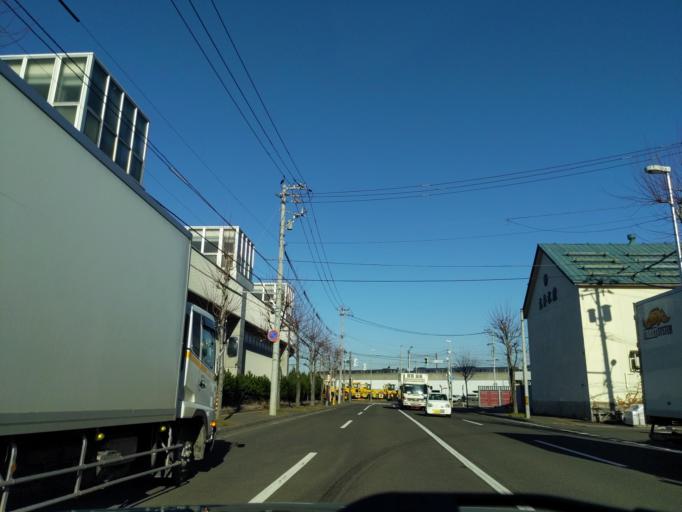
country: JP
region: Hokkaido
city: Sapporo
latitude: 43.0729
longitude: 141.3231
